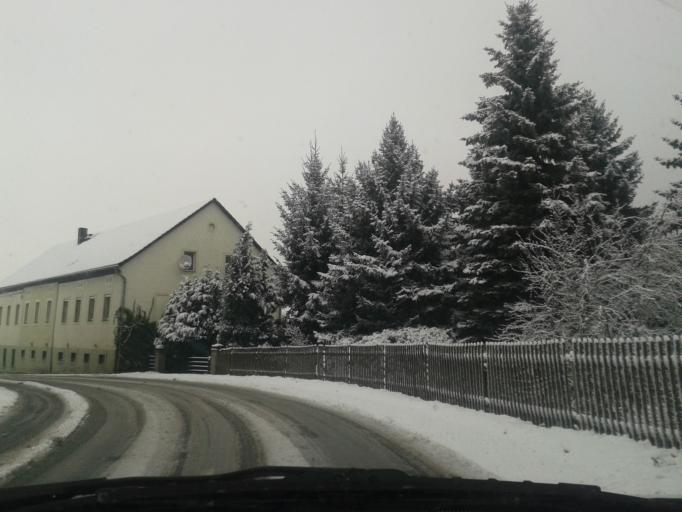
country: DE
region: Saxony
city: Durrrohrsdorf
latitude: 51.0164
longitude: 13.9539
